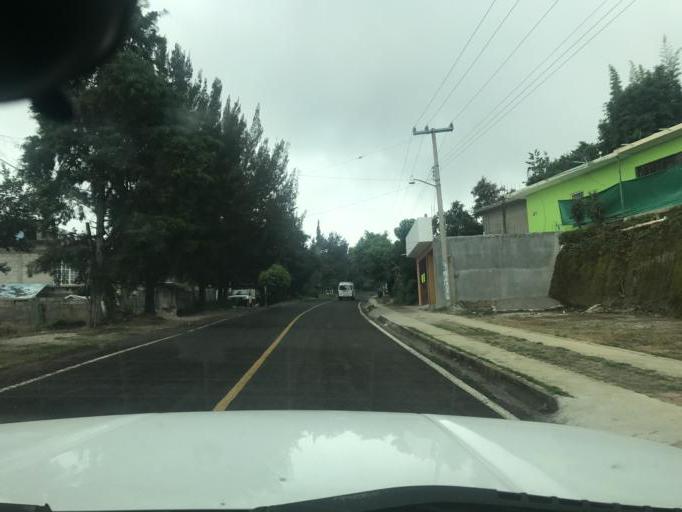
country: MX
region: Morelos
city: Ocuituco
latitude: 18.8811
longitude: -98.7701
